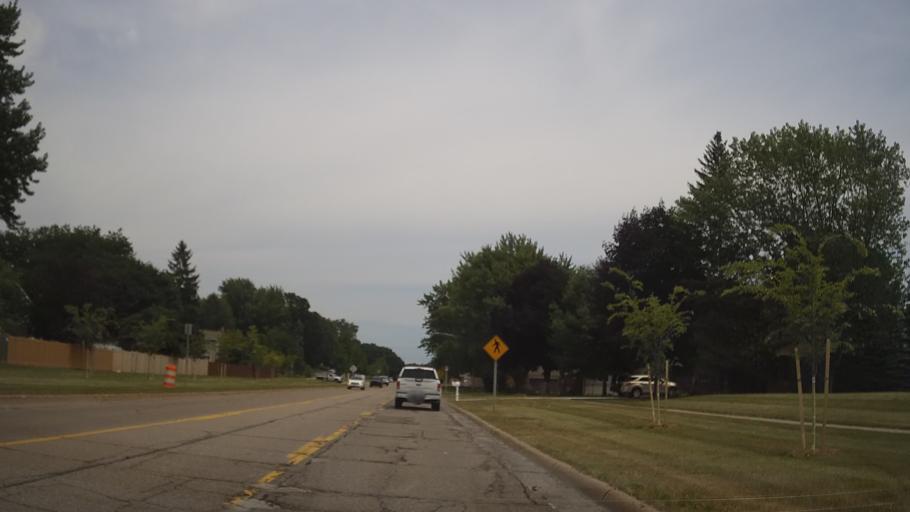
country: US
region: Michigan
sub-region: Macomb County
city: Sterling Heights
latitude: 42.5810
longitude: -83.0084
